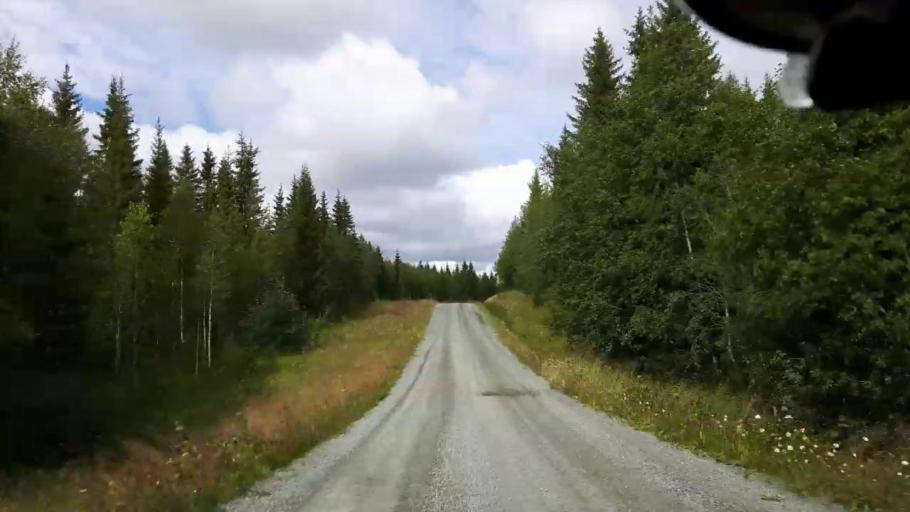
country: SE
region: Jaemtland
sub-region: Krokoms Kommun
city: Valla
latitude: 63.5591
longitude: 13.9163
